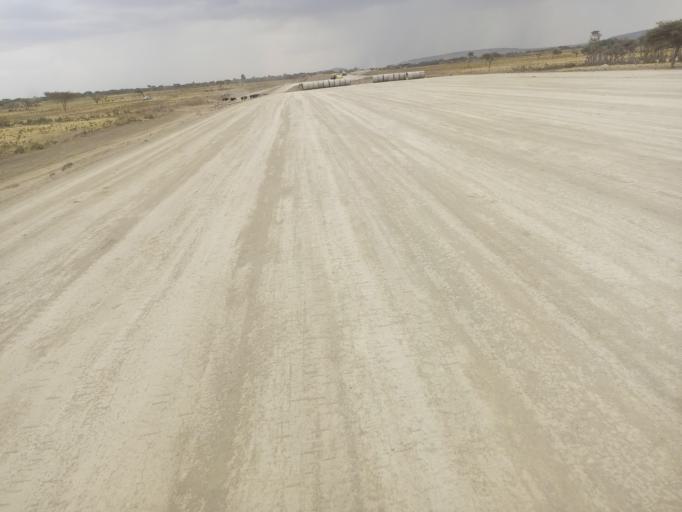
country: ET
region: Oromiya
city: Ziway
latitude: 7.8634
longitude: 38.6702
